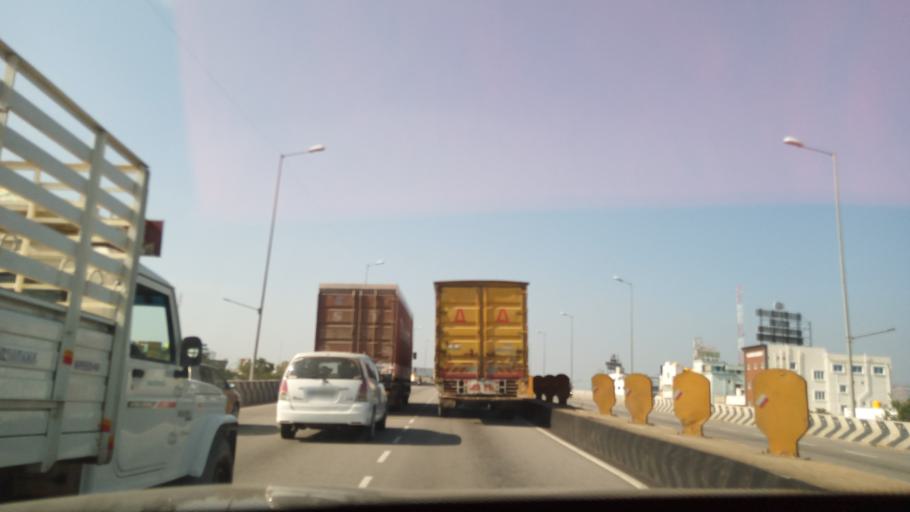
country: IN
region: Tamil Nadu
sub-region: Krishnagiri
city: Krishnagiri
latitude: 12.5281
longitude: 78.2077
